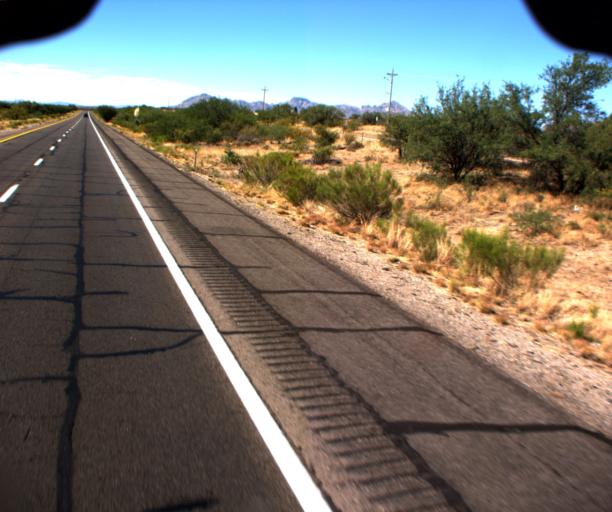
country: US
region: Arizona
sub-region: Pima County
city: Arivaca Junction
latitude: 31.6973
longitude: -111.0655
